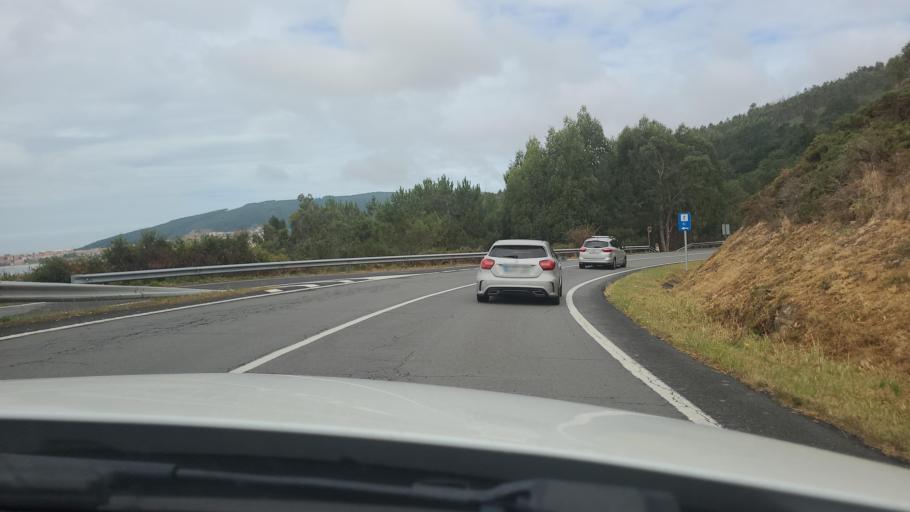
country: ES
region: Galicia
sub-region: Provincia da Coruna
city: Fisterra
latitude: 42.9286
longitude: -9.2384
